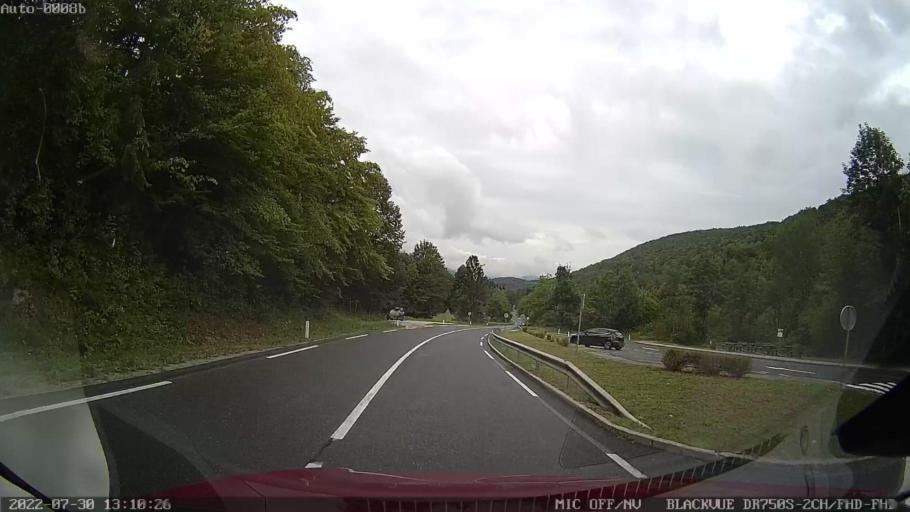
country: SI
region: Dolenjske Toplice
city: Dolenjske Toplice
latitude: 45.6943
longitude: 15.0865
